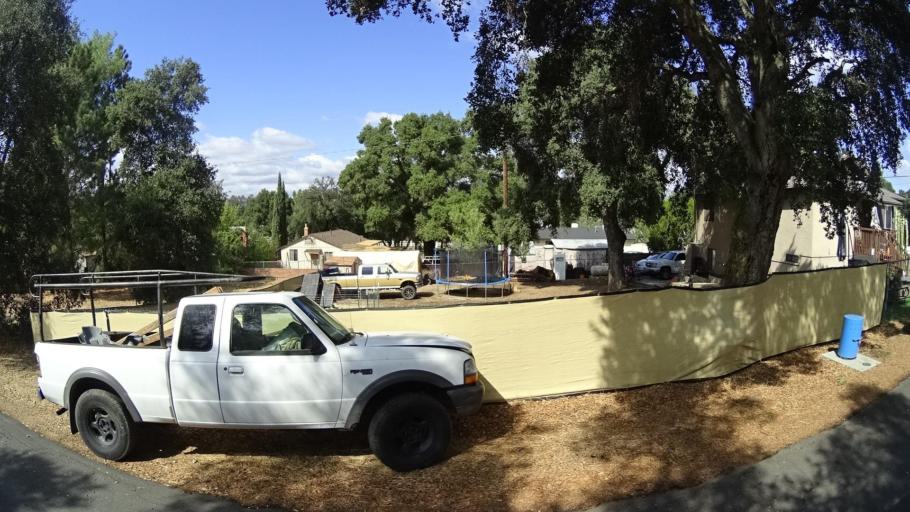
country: US
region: California
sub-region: San Diego County
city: Campo
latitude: 32.6810
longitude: -116.5112
